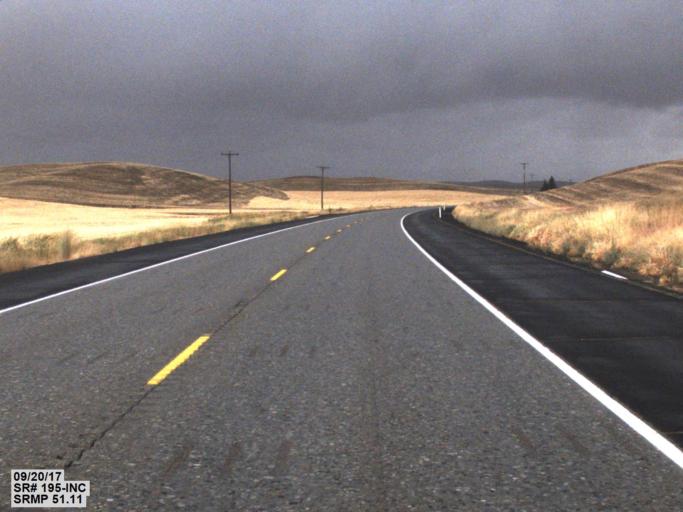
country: US
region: Washington
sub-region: Whitman County
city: Colfax
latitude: 47.0468
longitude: -117.3787
